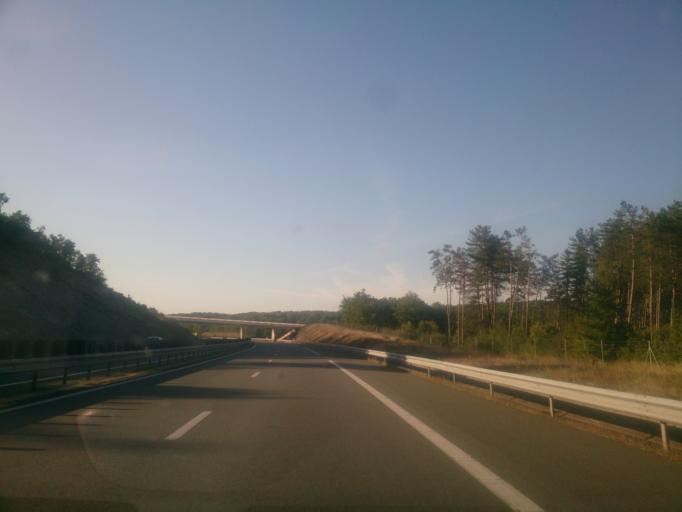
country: FR
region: Midi-Pyrenees
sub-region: Departement du Lot
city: Le Vigan
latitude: 44.7853
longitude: 1.5295
